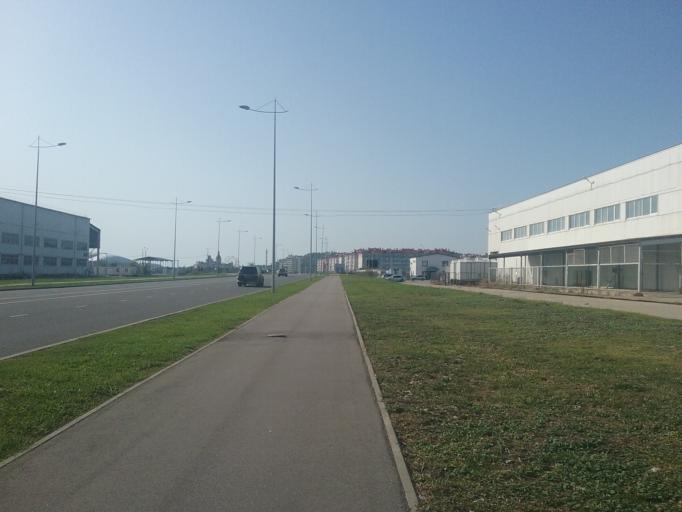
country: RU
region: Krasnodarskiy
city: Vysokoye
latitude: 43.3972
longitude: 39.9860
